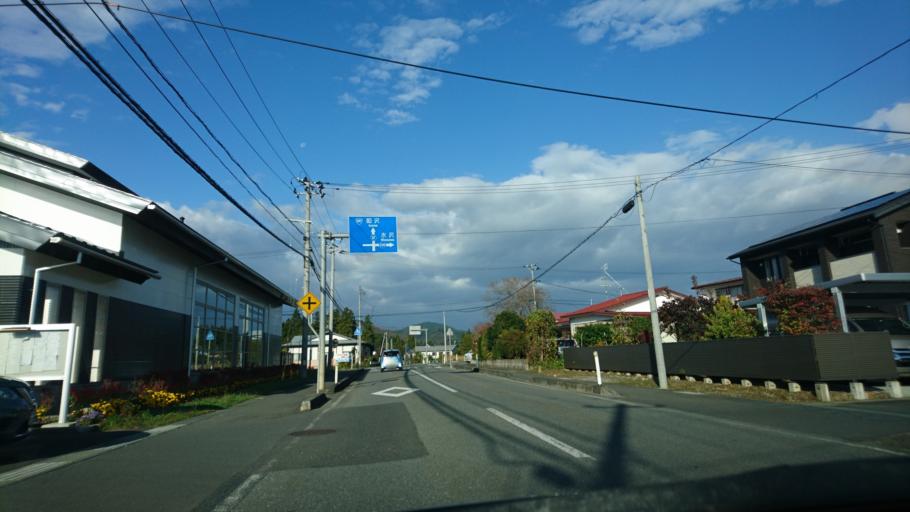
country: JP
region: Iwate
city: Mizusawa
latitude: 39.0393
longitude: 141.0638
